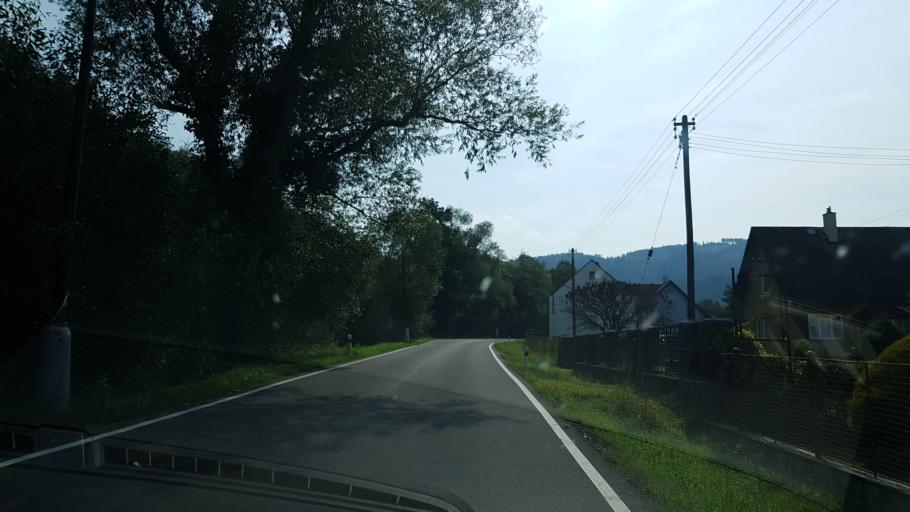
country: CZ
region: Olomoucky
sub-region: Okres Jesenik
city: Jesenik
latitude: 50.2154
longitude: 17.2197
